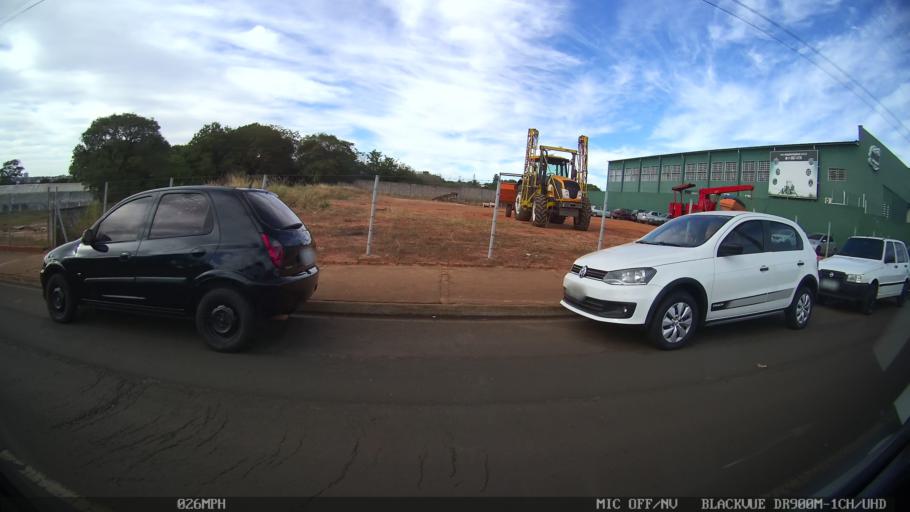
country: BR
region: Sao Paulo
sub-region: Catanduva
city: Catanduva
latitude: -21.1224
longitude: -48.9934
